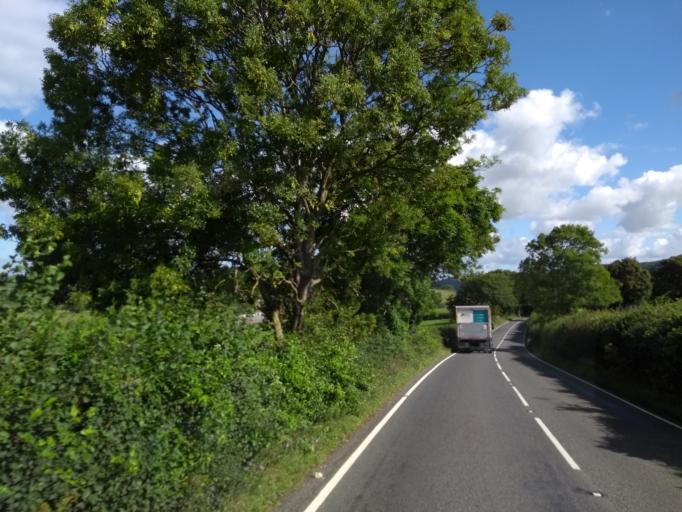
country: GB
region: England
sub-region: Somerset
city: Street
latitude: 51.0673
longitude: -2.7281
